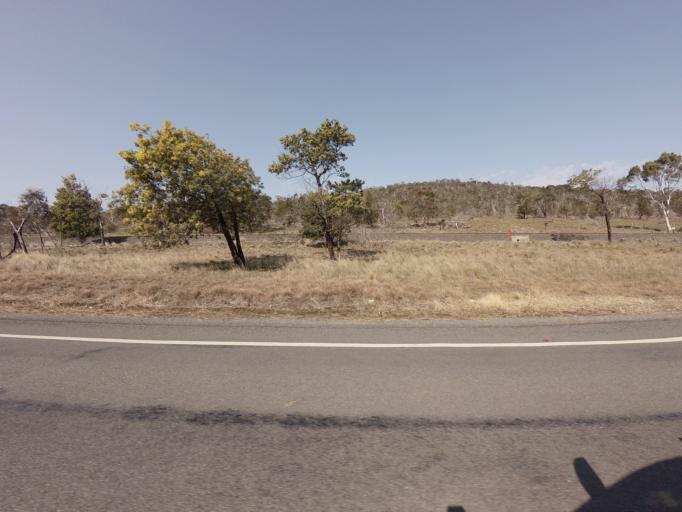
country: AU
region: Tasmania
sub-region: Northern Midlands
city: Evandale
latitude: -41.8103
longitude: 147.5941
